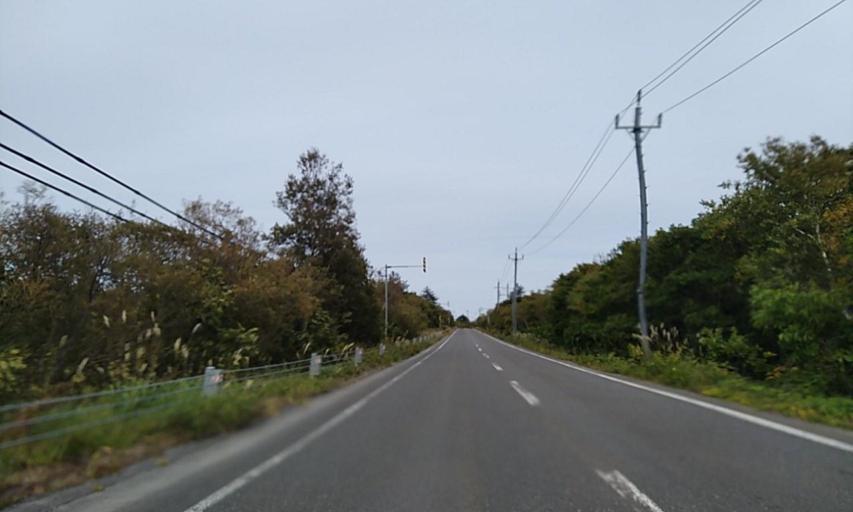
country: JP
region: Hokkaido
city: Makubetsu
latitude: 45.0012
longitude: 141.6977
